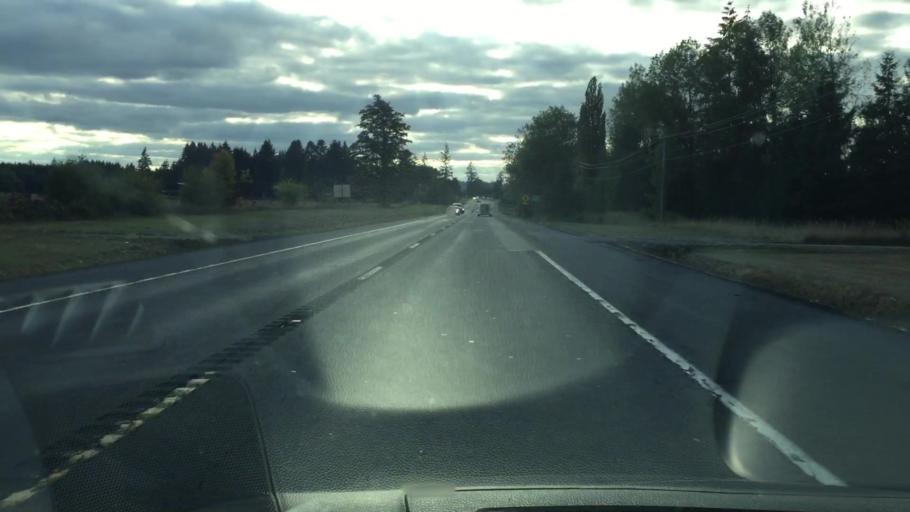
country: US
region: Washington
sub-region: Lewis County
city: Napavine
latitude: 46.5322
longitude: -122.7340
